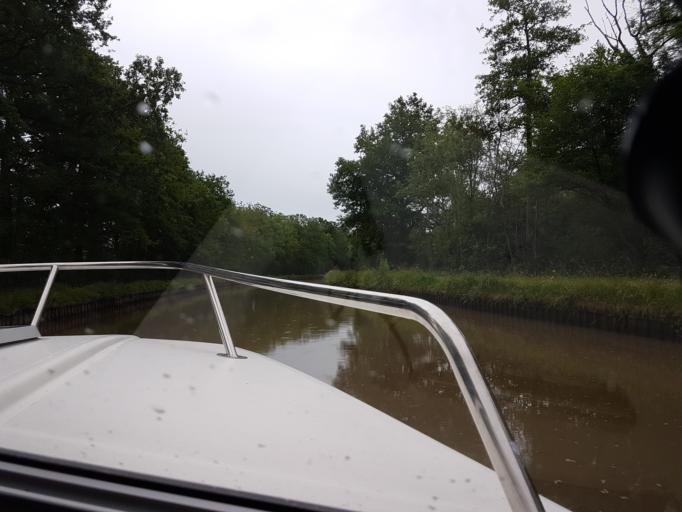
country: FR
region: Bourgogne
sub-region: Departement de la Nievre
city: Clamecy
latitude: 47.3718
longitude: 3.6078
